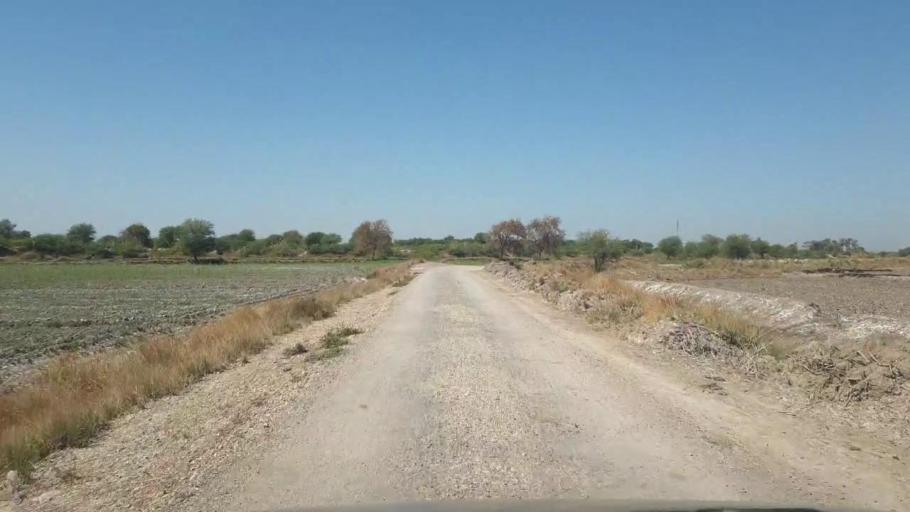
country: PK
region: Sindh
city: Dhoro Naro
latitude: 25.4518
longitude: 69.6092
